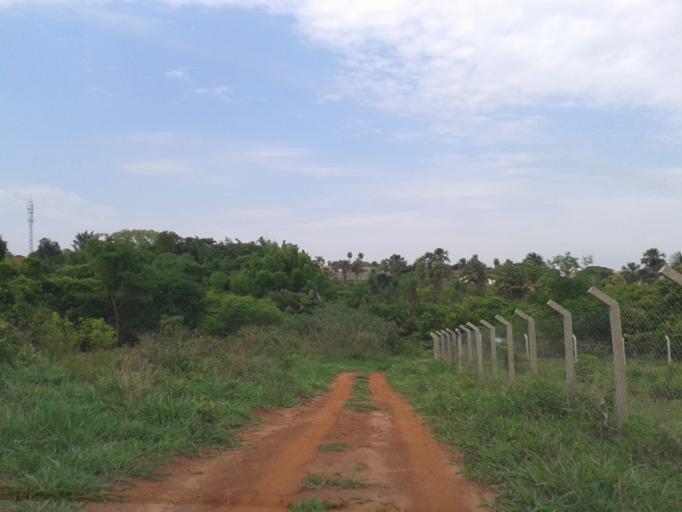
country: BR
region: Minas Gerais
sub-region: Ituiutaba
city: Ituiutaba
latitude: -18.9824
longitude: -49.4426
